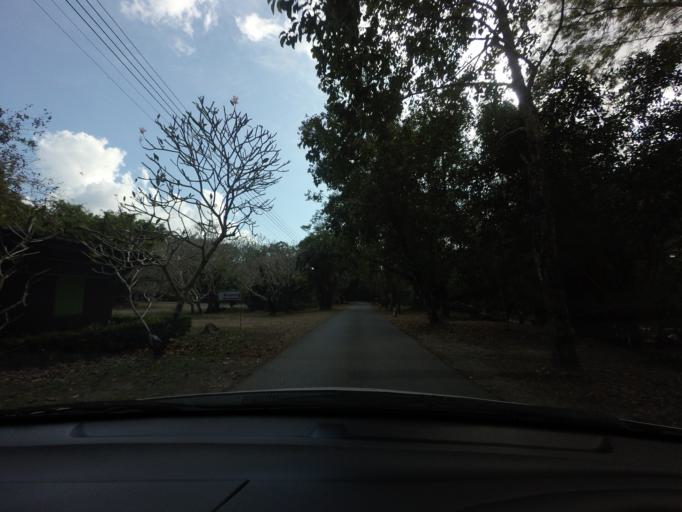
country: TH
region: Nakhon Nayok
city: Nakhon Nayok
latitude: 14.3330
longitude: 101.3057
